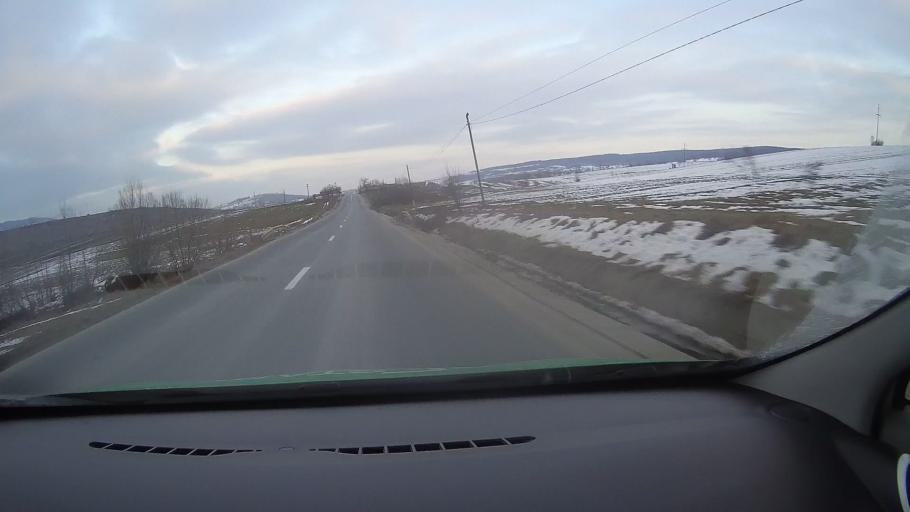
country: RO
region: Harghita
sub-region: Comuna Lupeni
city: Lupeni
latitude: 46.3566
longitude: 25.2090
